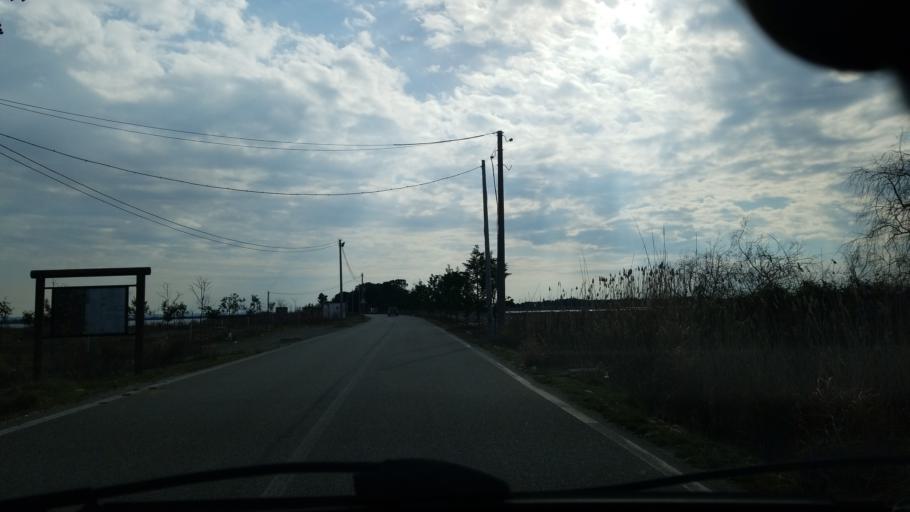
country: AL
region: Lezhe
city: Shengjin
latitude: 41.7718
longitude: 19.6015
